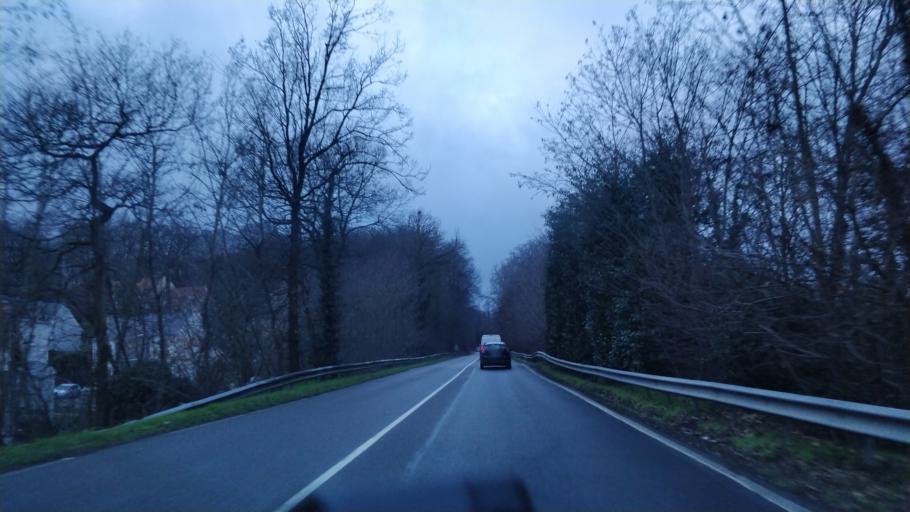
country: FR
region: Ile-de-France
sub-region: Departement de l'Essonne
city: Bures-sur-Yvette
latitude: 48.6923
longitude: 2.1764
